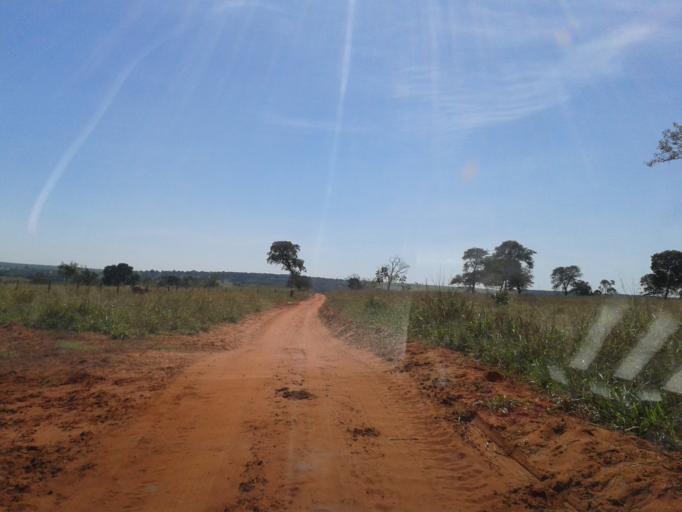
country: BR
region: Minas Gerais
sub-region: Santa Vitoria
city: Santa Vitoria
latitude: -19.0144
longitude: -50.3245
